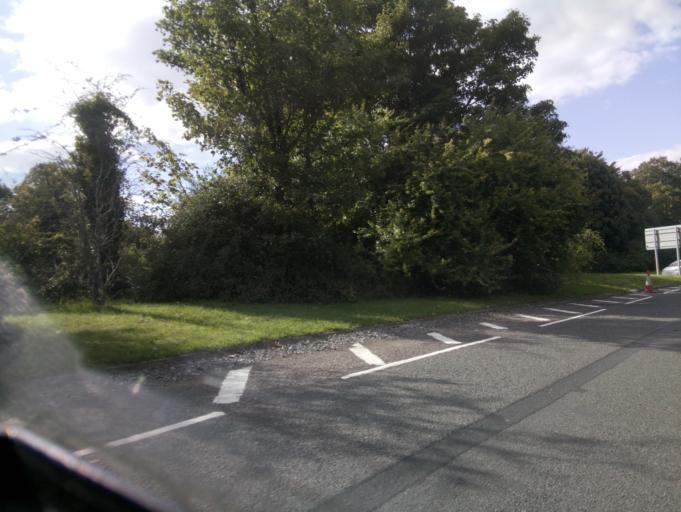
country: GB
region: England
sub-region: Hampshire
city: Compton
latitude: 51.0511
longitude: -1.3497
